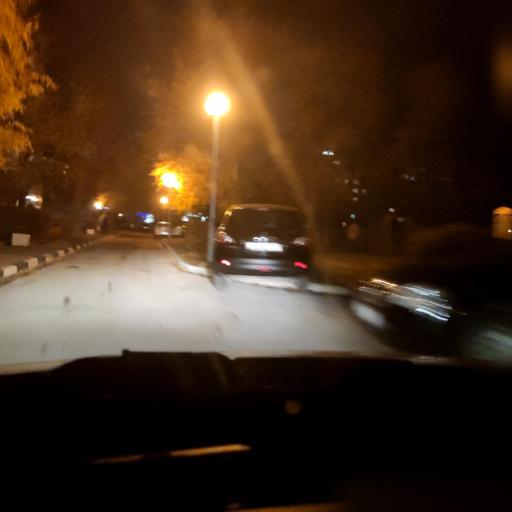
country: RU
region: Samara
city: Tol'yatti
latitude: 53.5358
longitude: 49.3160
